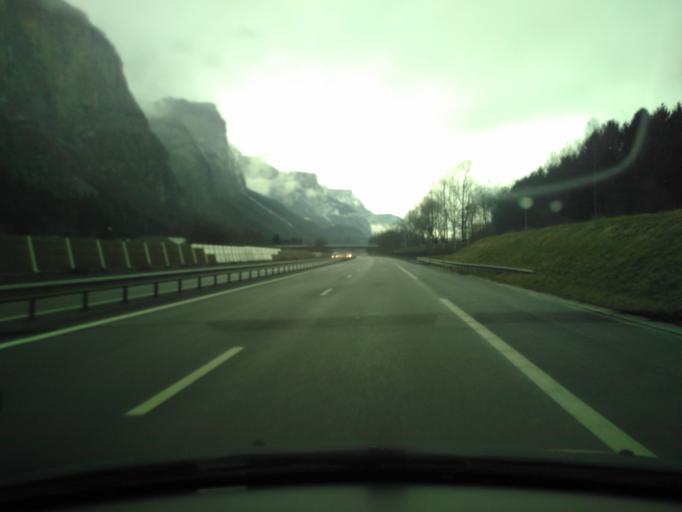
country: FR
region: Rhone-Alpes
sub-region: Departement de la Haute-Savoie
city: Magland
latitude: 46.0240
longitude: 6.6166
